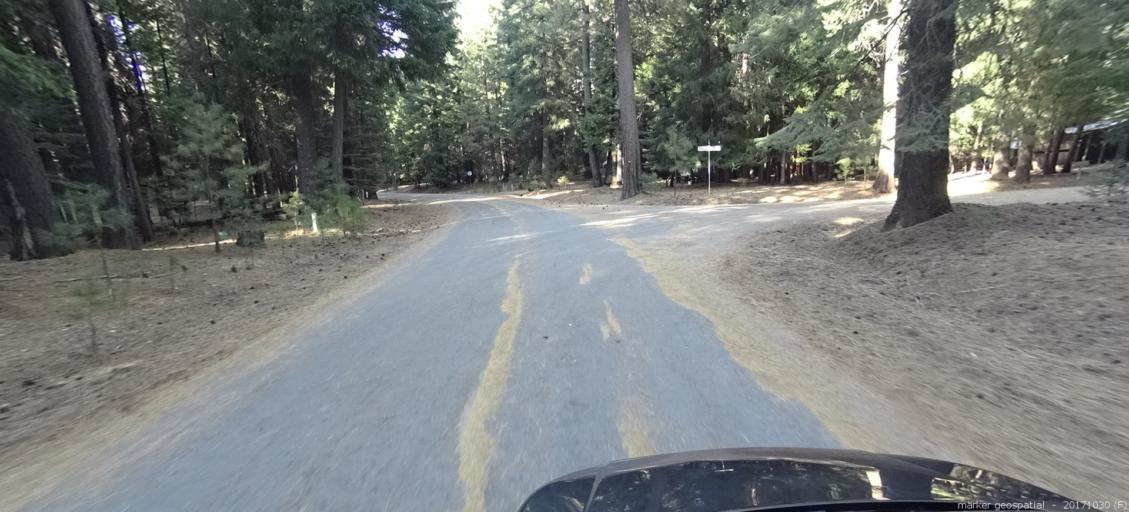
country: US
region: California
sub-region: Shasta County
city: Shingletown
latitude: 40.5547
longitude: -121.7312
